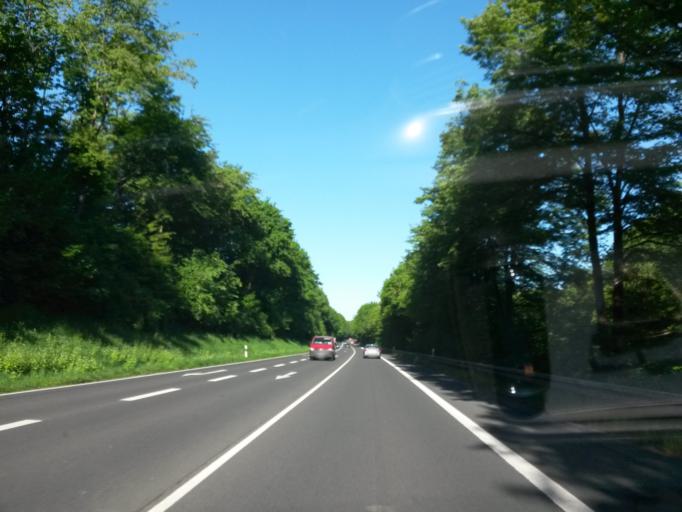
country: DE
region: North Rhine-Westphalia
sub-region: Regierungsbezirk Koln
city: Siegburg
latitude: 50.8121
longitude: 7.2313
